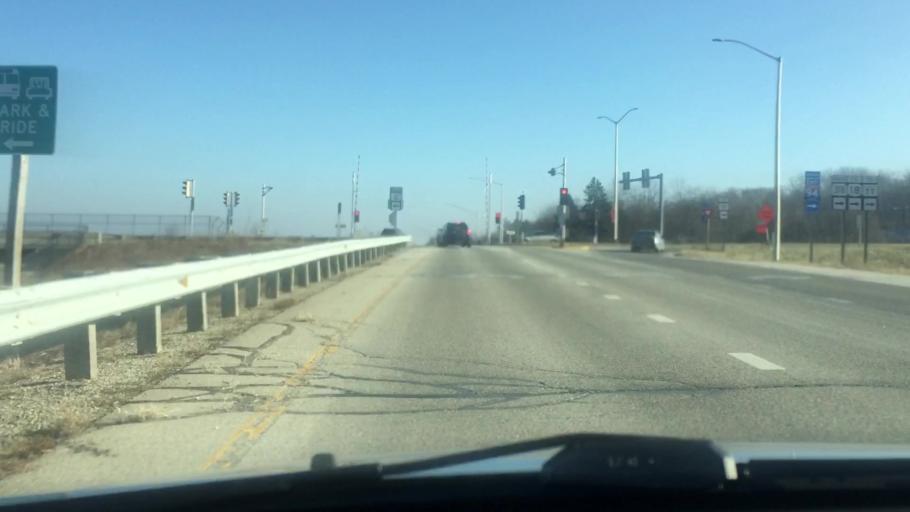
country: US
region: Wisconsin
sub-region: Waukesha County
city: Pewaukee
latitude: 43.0487
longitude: -88.2866
